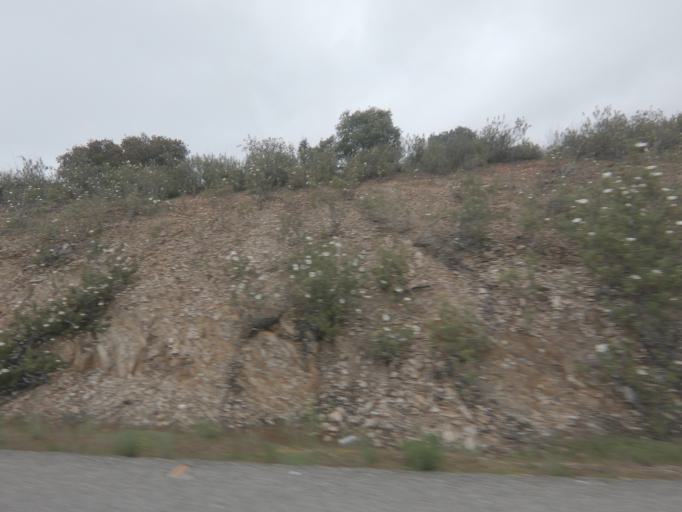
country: ES
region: Extremadura
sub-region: Provincia de Badajoz
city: Puebla de Obando
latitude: 39.2627
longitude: -6.5466
